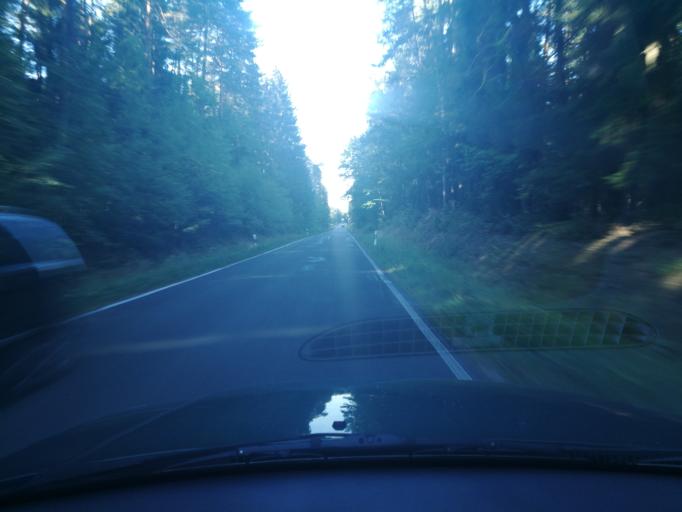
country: DE
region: Bavaria
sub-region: Regierungsbezirk Mittelfranken
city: Hessdorf
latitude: 49.6111
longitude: 10.9379
